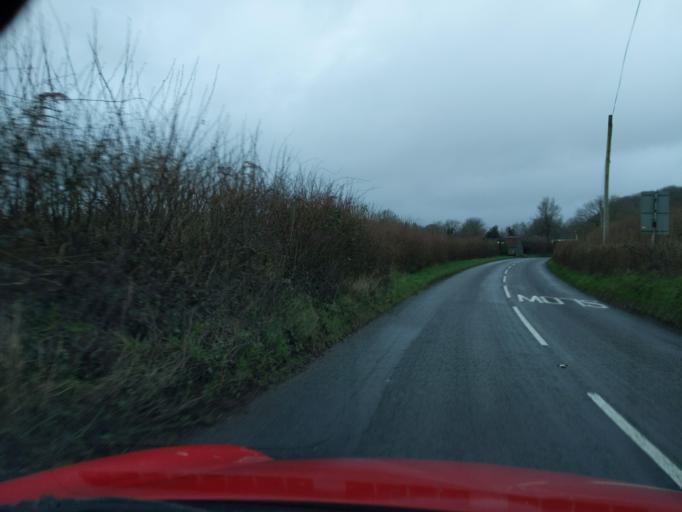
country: GB
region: England
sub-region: Cornwall
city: Werrington
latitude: 50.6980
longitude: -4.3224
